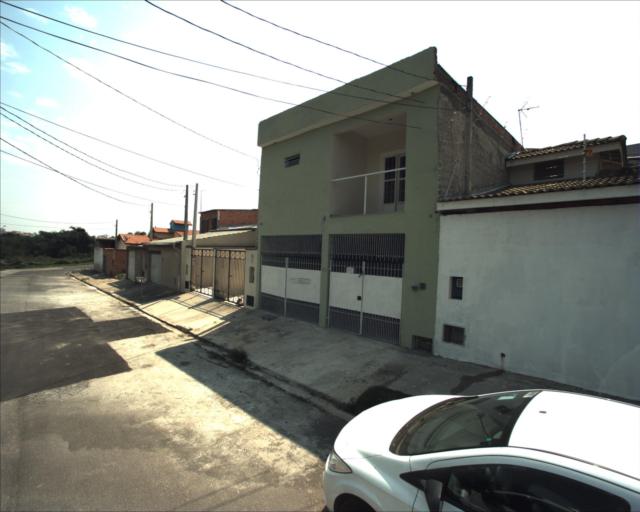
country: BR
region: Sao Paulo
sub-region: Sorocaba
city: Sorocaba
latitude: -23.4426
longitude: -47.4872
